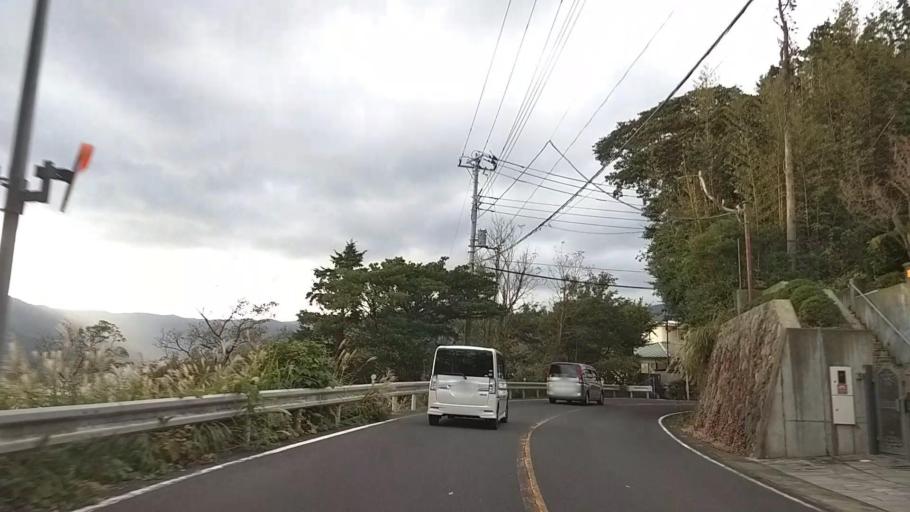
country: JP
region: Kanagawa
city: Yugawara
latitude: 35.1507
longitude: 139.1391
